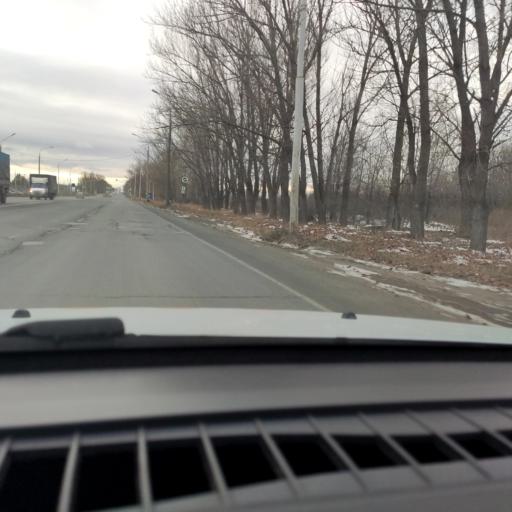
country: RU
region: Samara
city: Podstepki
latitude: 53.5715
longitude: 49.2181
